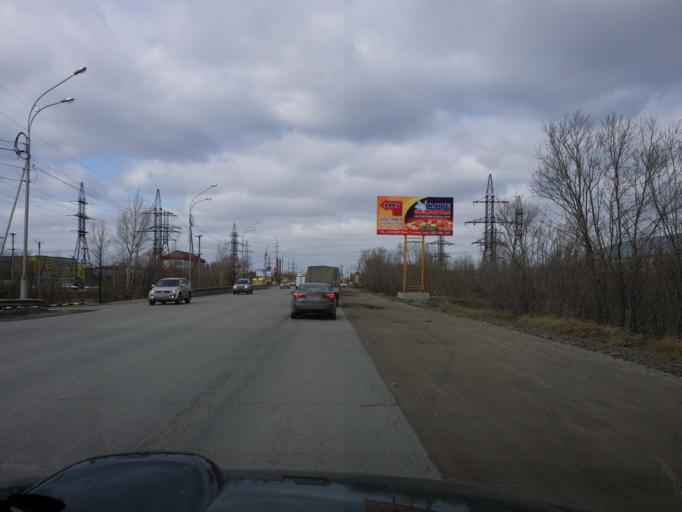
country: RU
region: Khanty-Mansiyskiy Avtonomnyy Okrug
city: Nizhnevartovsk
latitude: 60.9315
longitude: 76.5313
